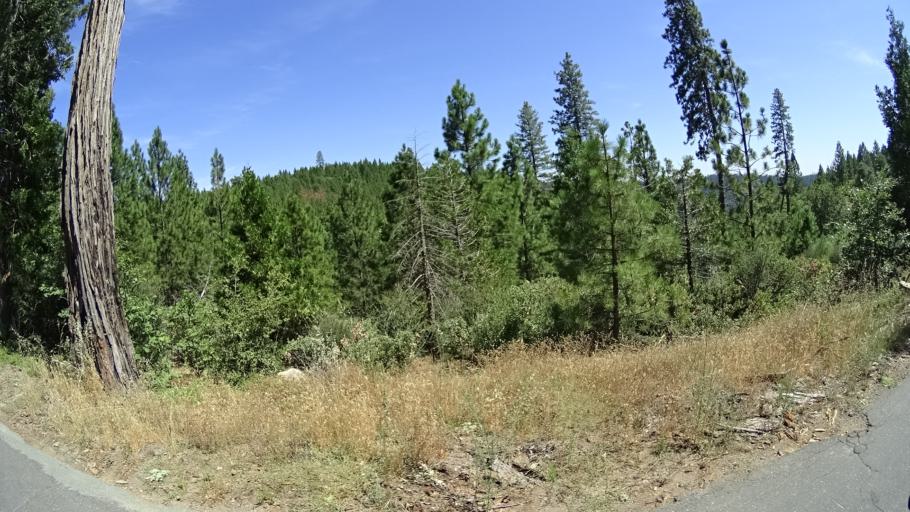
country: US
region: California
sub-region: Calaveras County
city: Forest Meadows
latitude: 38.1955
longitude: -120.4034
